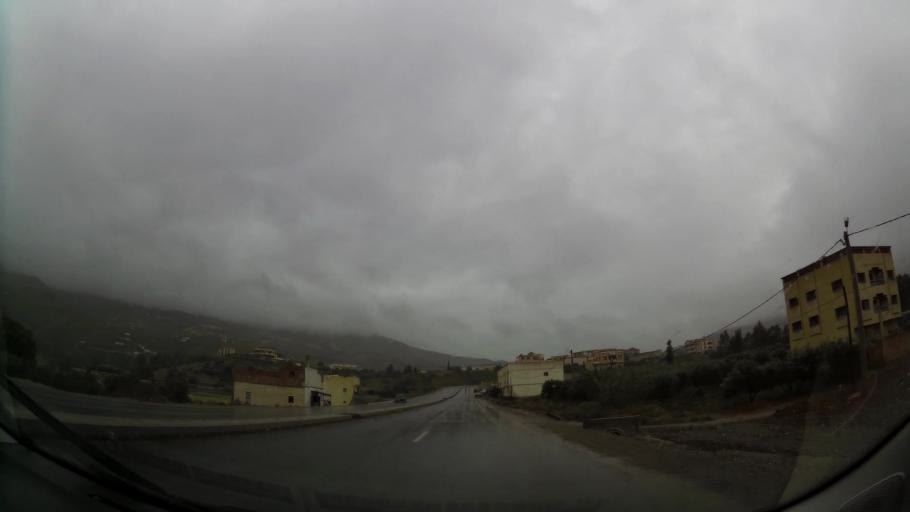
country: MA
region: Taza-Al Hoceima-Taounate
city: Imzourene
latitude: 35.0426
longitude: -3.8230
